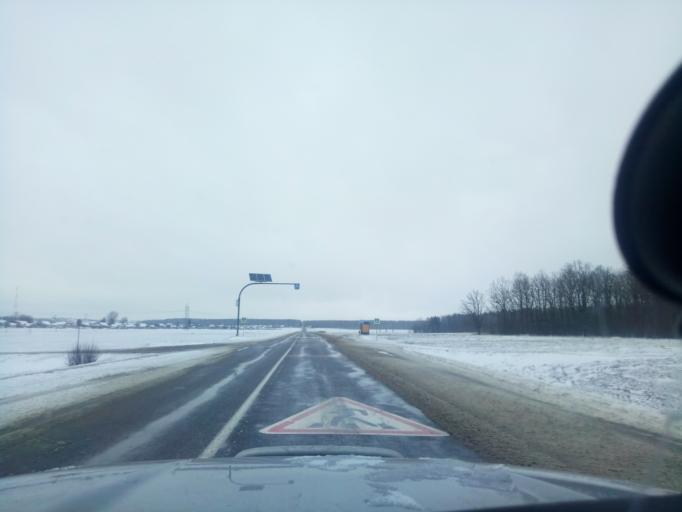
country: BY
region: Minsk
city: Kapyl'
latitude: 53.1148
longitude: 27.0633
